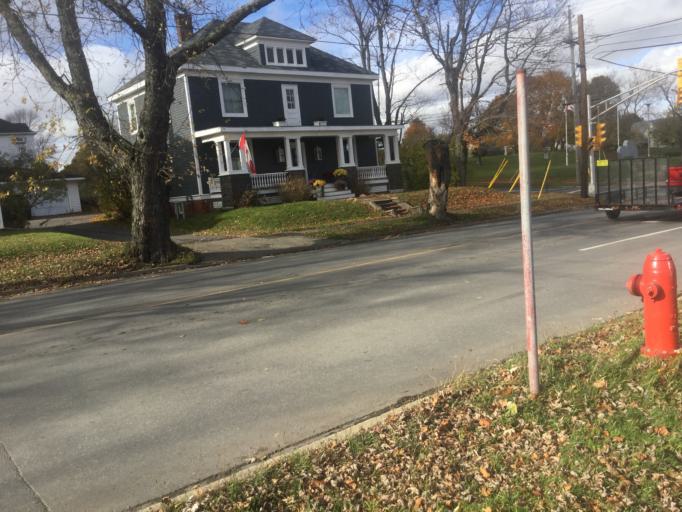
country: CA
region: Nova Scotia
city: New Glasgow
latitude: 45.5621
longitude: -62.6595
